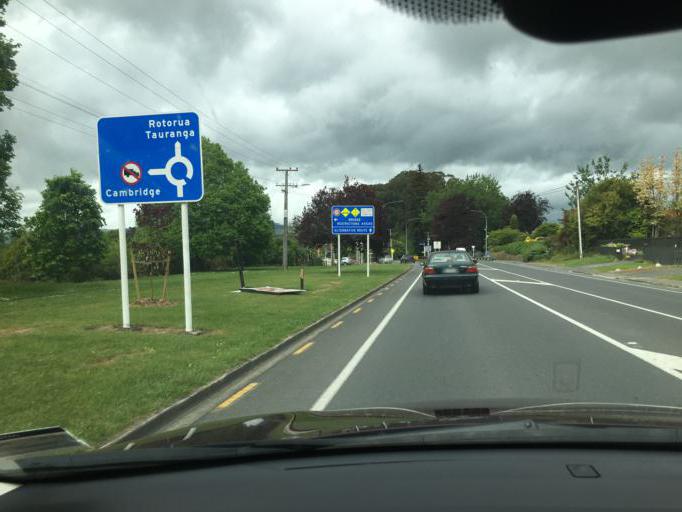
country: NZ
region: Waikato
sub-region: Waipa District
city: Cambridge
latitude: -37.9003
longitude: 175.4731
